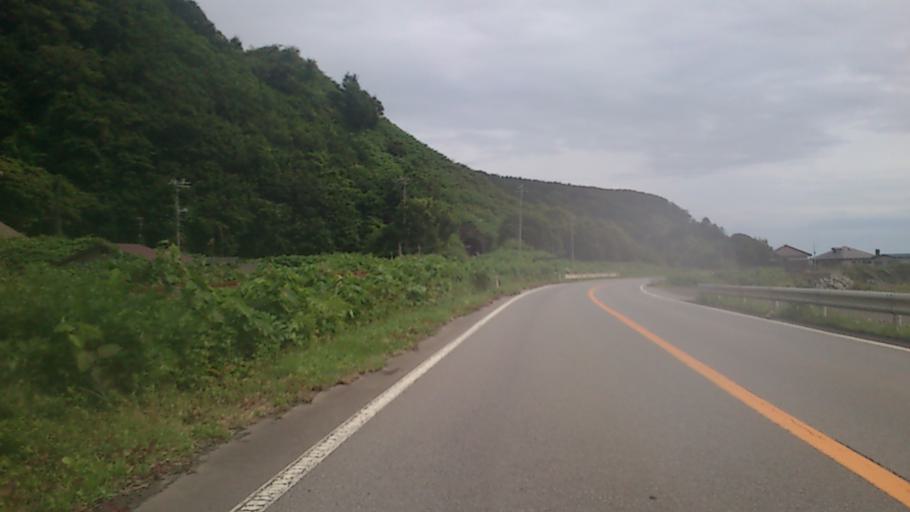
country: JP
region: Akita
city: Noshiromachi
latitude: 40.4543
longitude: 139.9426
